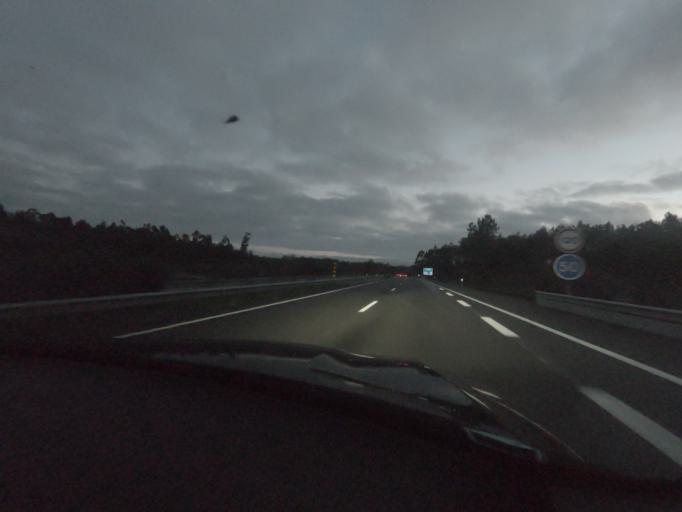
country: PT
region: Leiria
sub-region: Pombal
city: Pombal
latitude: 39.9346
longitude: -8.6805
